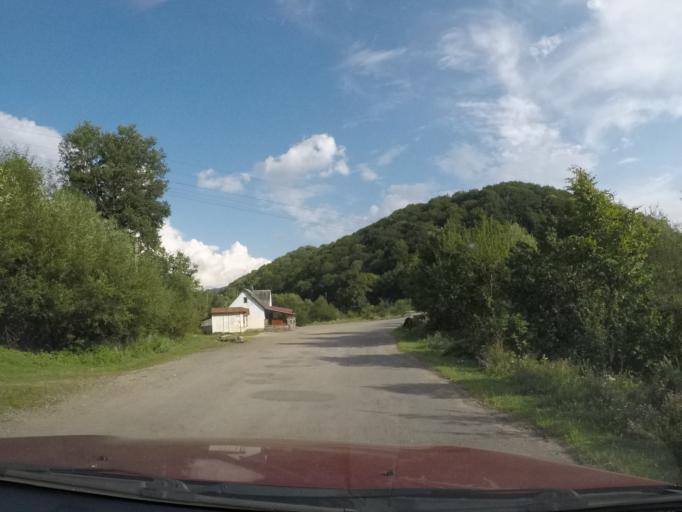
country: UA
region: Zakarpattia
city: Velykyi Bereznyi
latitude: 49.0041
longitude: 22.6394
